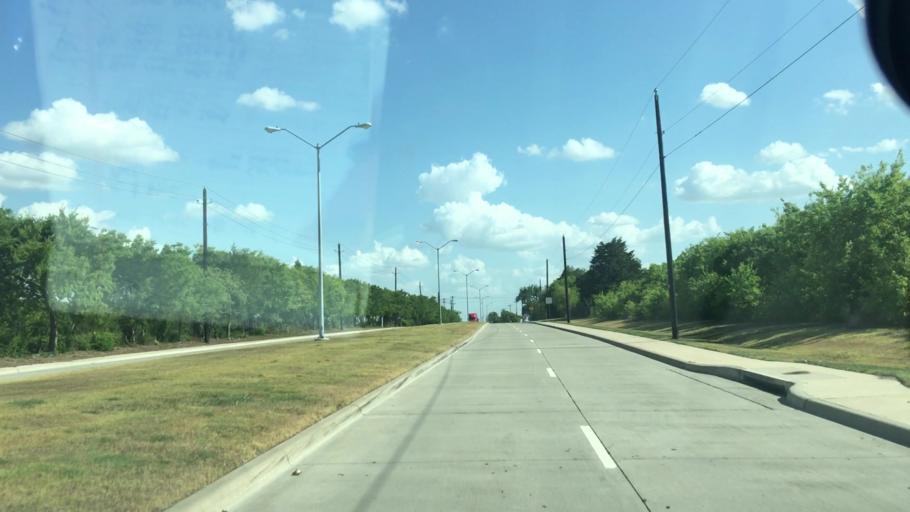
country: US
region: Texas
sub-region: Dallas County
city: Lancaster
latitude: 32.6217
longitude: -96.7532
